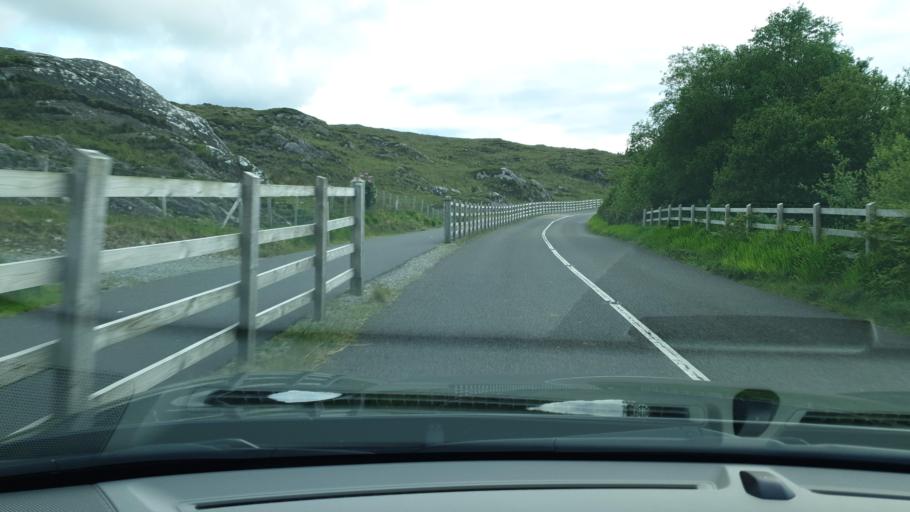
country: IE
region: Connaught
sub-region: County Galway
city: Clifden
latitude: 53.4553
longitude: -9.8256
